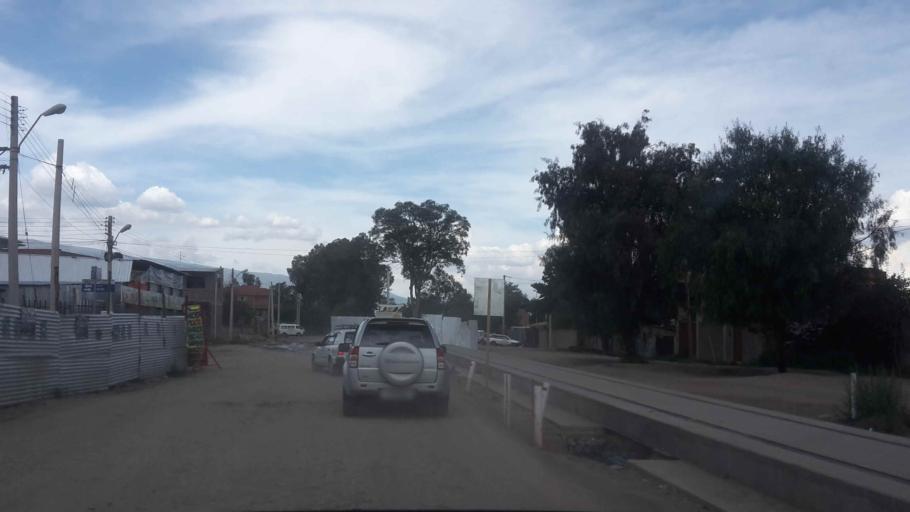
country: BO
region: Cochabamba
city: Cochabamba
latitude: -17.4011
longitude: -66.2750
